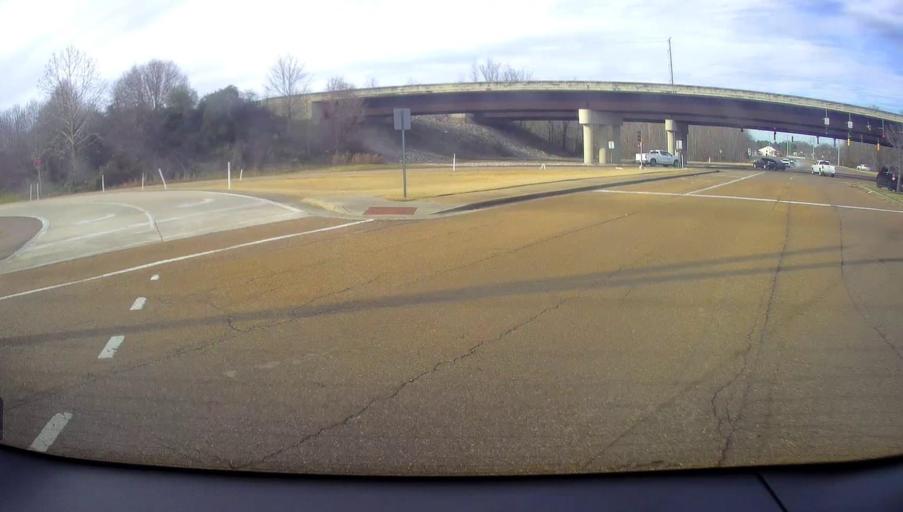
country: US
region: Tennessee
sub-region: Shelby County
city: Collierville
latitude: 35.0252
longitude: -89.7224
